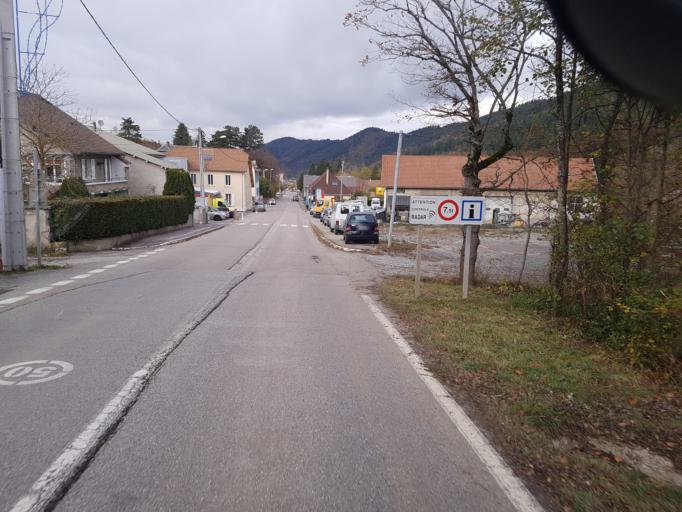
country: FR
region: Rhone-Alpes
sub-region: Departement de l'Isere
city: La Motte-Saint-Martin
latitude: 44.9100
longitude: 5.6312
